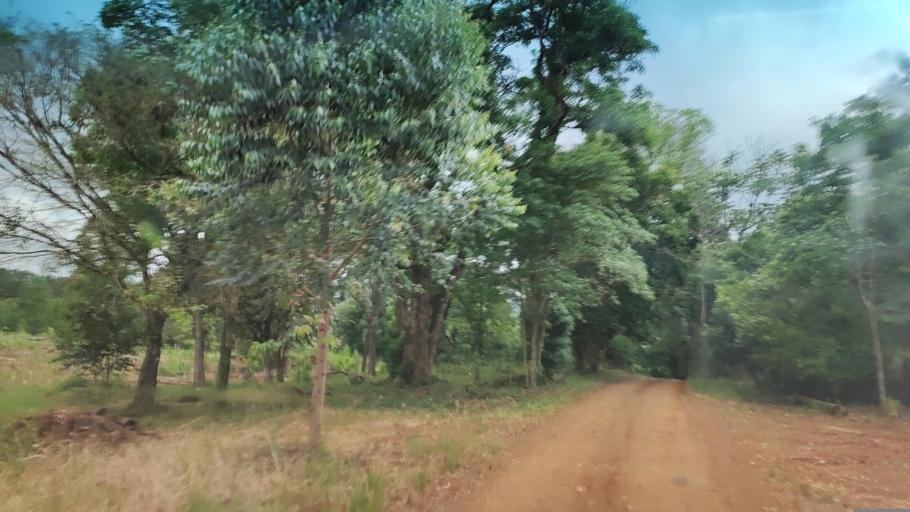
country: AR
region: Misiones
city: Dos de Mayo
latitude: -27.0072
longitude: -54.6224
